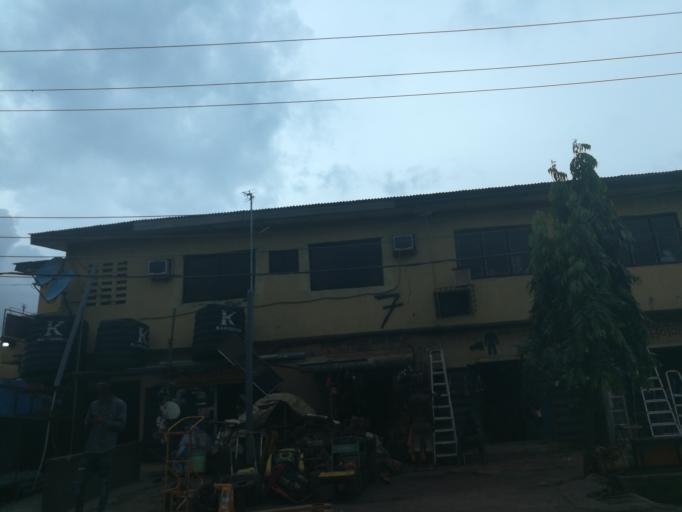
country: NG
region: Lagos
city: Agege
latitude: 6.6190
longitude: 3.3364
